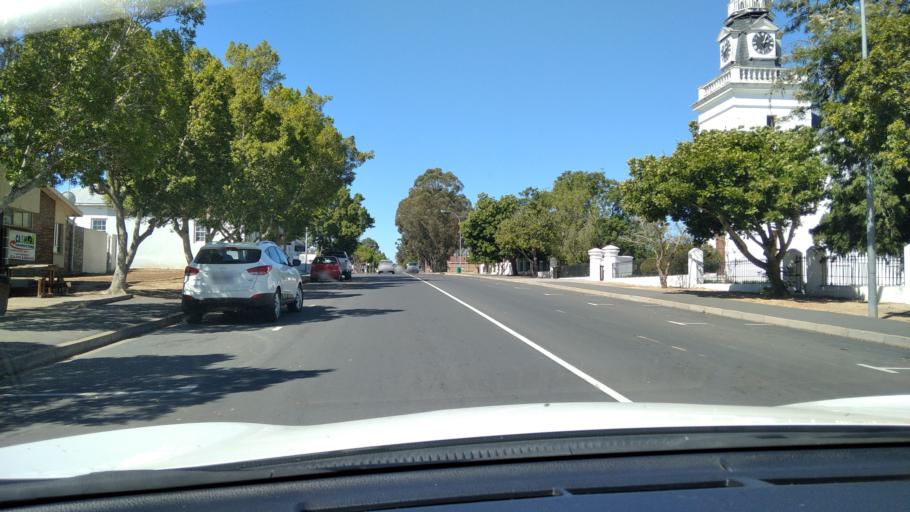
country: ZA
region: Western Cape
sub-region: West Coast District Municipality
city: Moorreesburg
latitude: -33.0626
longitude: 18.3480
